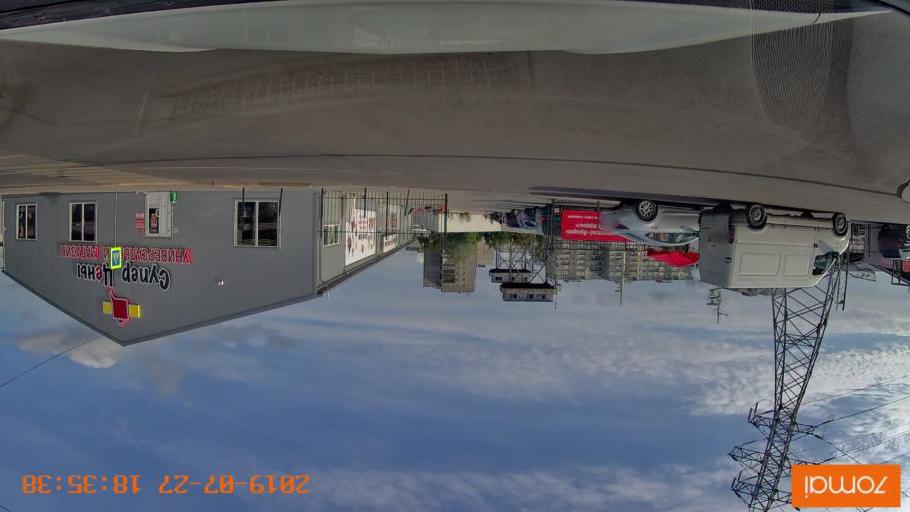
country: RU
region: Kaliningrad
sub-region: Gorod Kaliningrad
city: Kaliningrad
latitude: 54.7049
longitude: 20.4981
